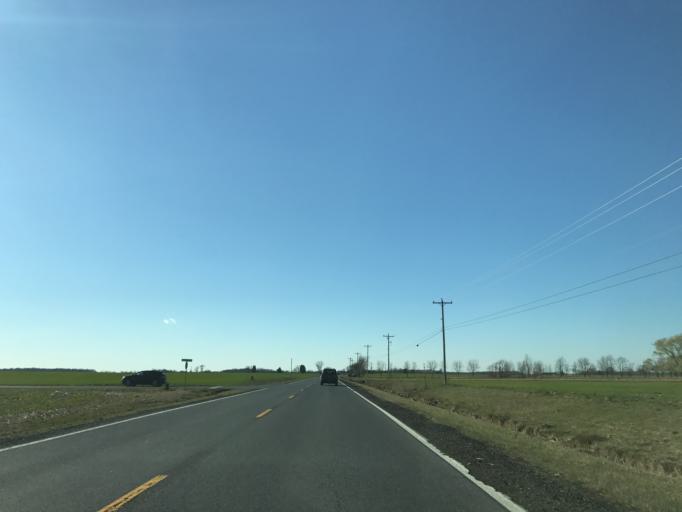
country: US
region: Maryland
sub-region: Queen Anne's County
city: Centreville
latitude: 39.0076
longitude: -75.9846
